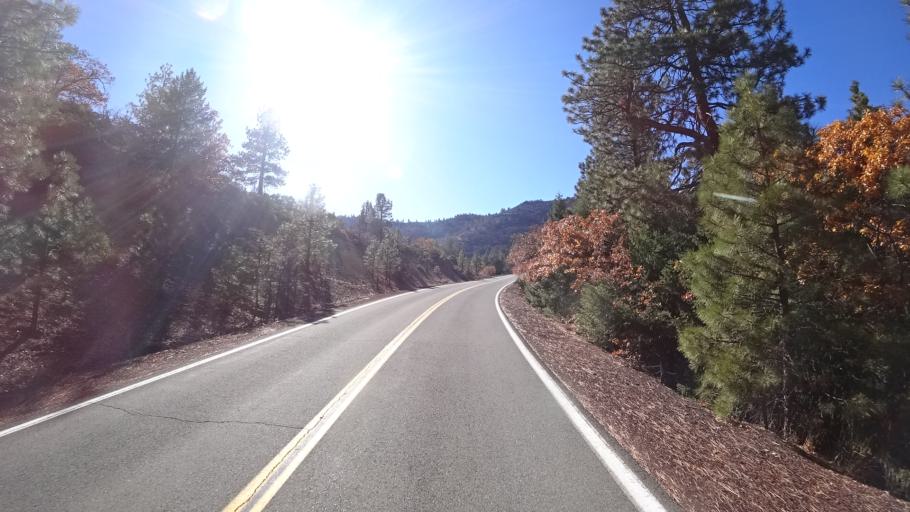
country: US
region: California
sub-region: Siskiyou County
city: Weed
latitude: 41.4528
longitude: -122.6444
